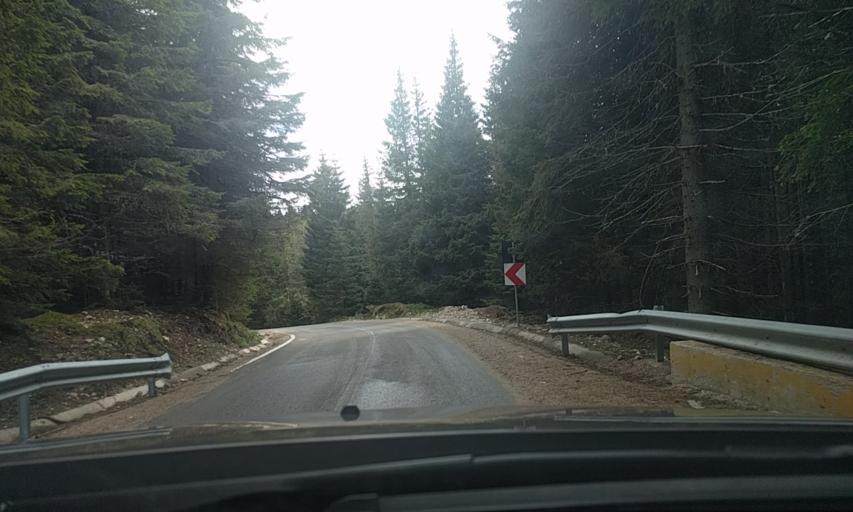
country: RO
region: Prahova
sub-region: Oras Busteni
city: Busteni
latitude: 45.3893
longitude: 25.4390
